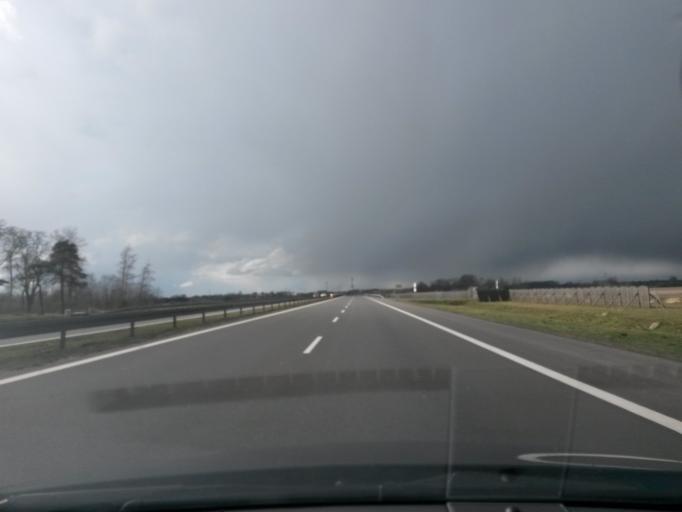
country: PL
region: Greater Poland Voivodeship
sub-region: Powiat poznanski
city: Kleszczewo
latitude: 52.3251
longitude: 17.1048
